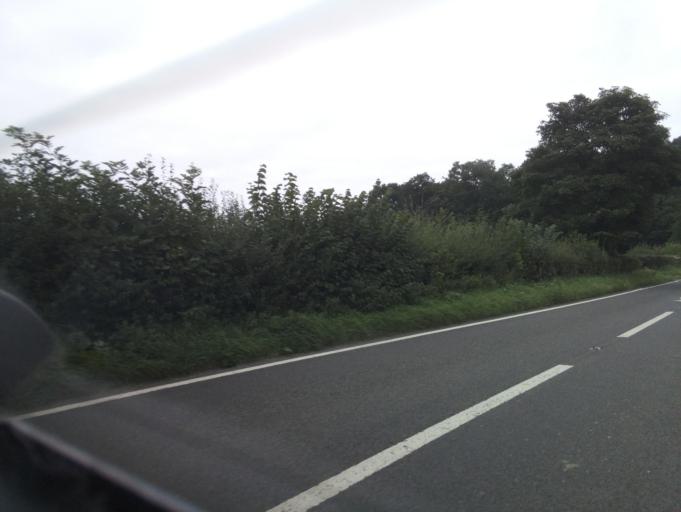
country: GB
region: England
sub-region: Derbyshire
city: Bradley
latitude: 53.0161
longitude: -1.6673
